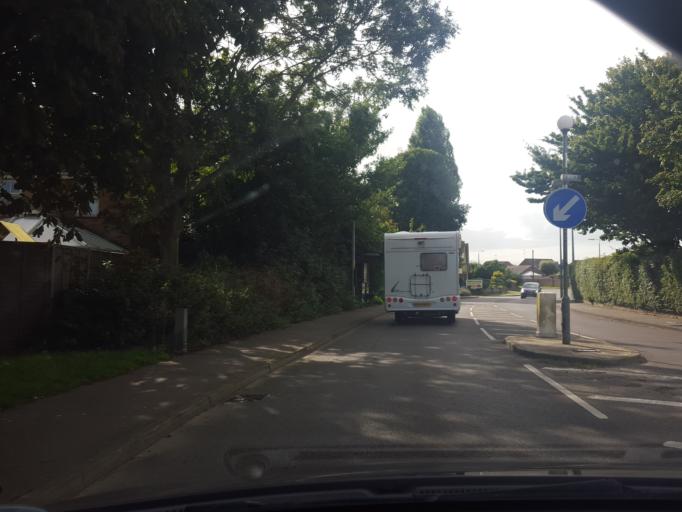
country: GB
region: England
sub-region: Essex
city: Dovercourt
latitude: 51.9267
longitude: 1.2614
